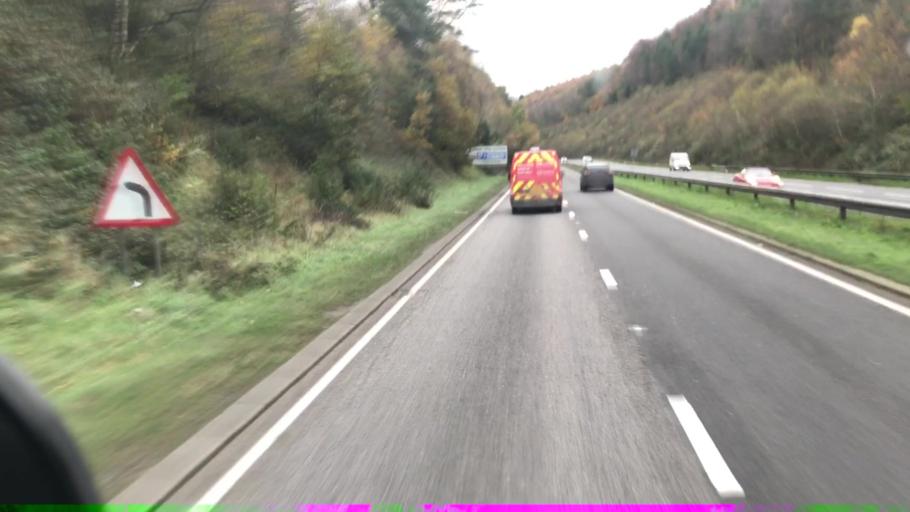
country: GB
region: England
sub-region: Devon
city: Chudleigh
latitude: 50.6456
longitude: -3.5537
